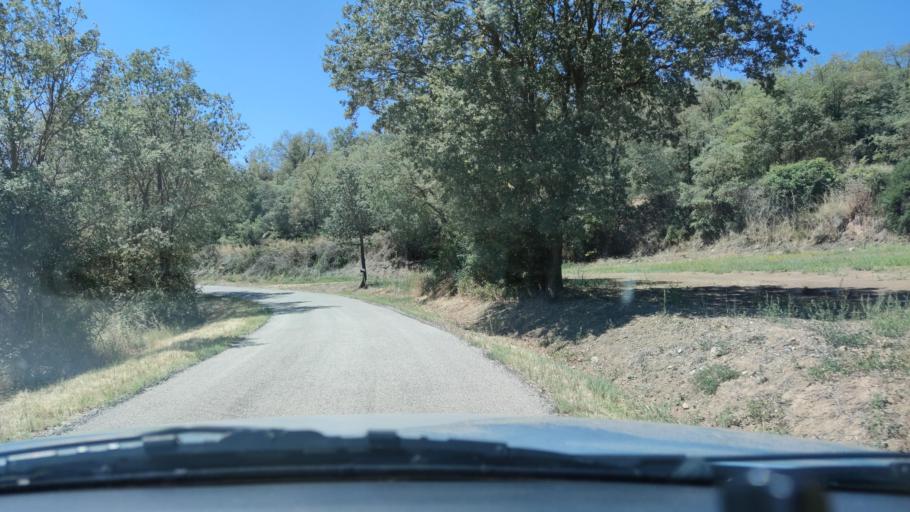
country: ES
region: Catalonia
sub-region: Provincia de Lleida
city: Tora de Riubregos
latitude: 41.8787
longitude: 1.4344
